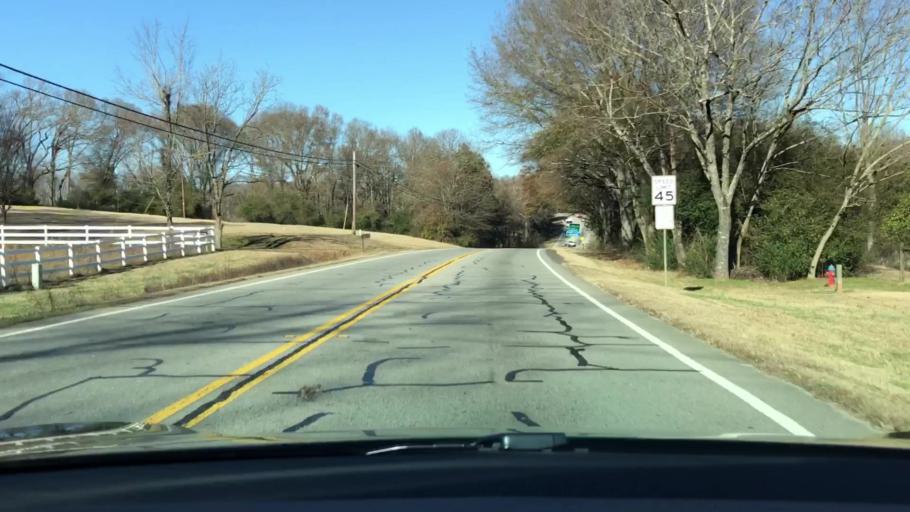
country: US
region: Georgia
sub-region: Barrow County
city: Russell
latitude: 33.9247
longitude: -83.7154
